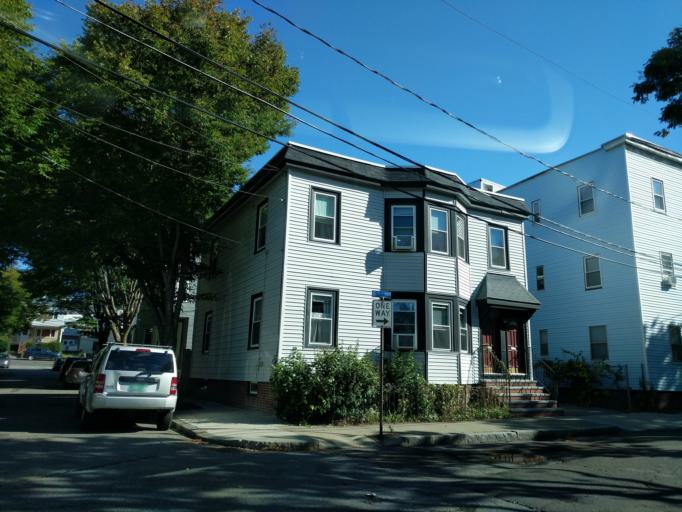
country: US
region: Massachusetts
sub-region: Middlesex County
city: Somerville
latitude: 42.3829
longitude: -71.1031
